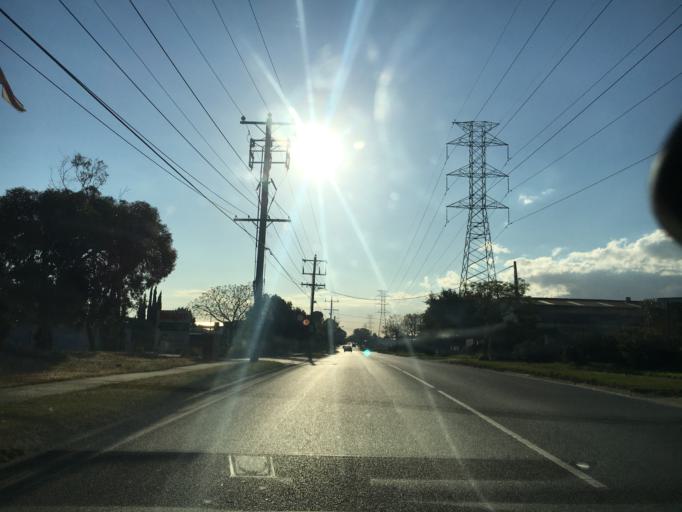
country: AU
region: Victoria
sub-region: Kingston
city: Clayton South
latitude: -37.9418
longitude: 145.1282
